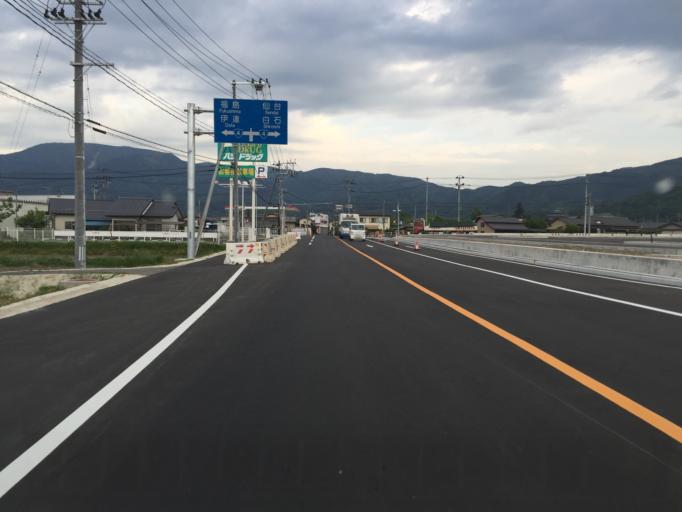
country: JP
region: Fukushima
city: Hobaramachi
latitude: 37.8717
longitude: 140.5460
